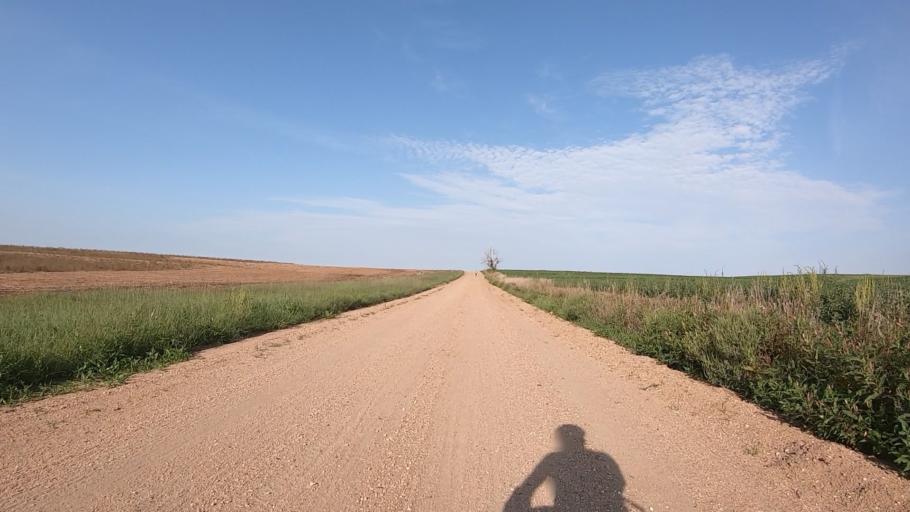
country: US
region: Kansas
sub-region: Marshall County
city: Blue Rapids
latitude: 39.6570
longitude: -96.8641
